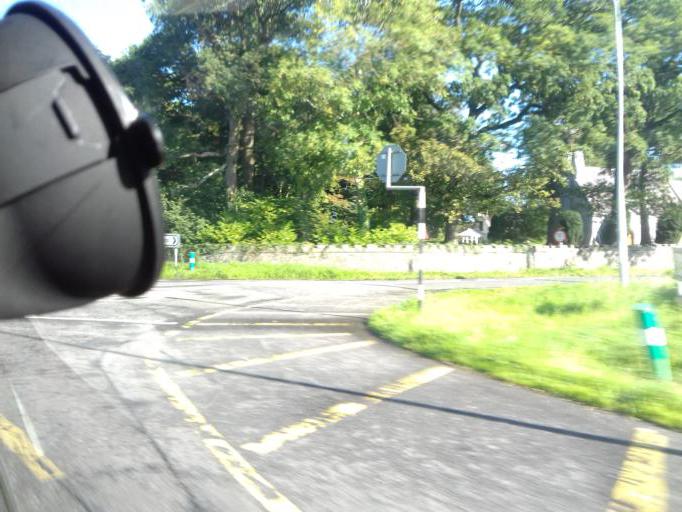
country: IE
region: Leinster
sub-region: Uibh Fhaili
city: Tullamore
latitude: 53.3151
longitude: -7.5089
